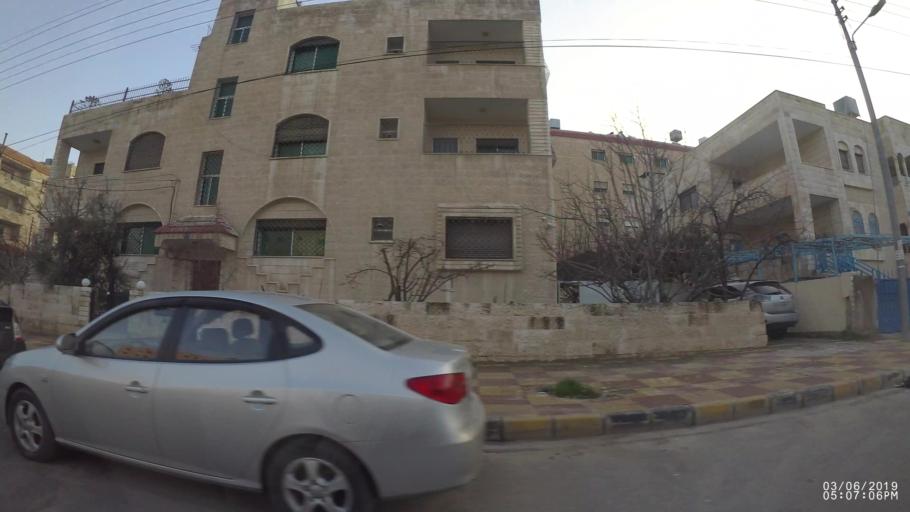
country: JO
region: Amman
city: Amman
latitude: 31.9915
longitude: 35.9484
